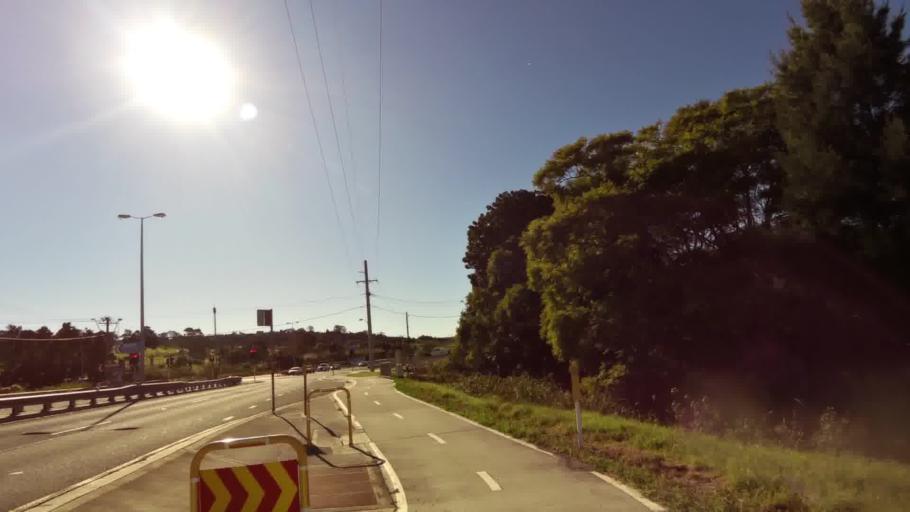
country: AU
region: New South Wales
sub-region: Wollongong
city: Koonawarra
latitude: -34.4711
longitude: 150.8175
